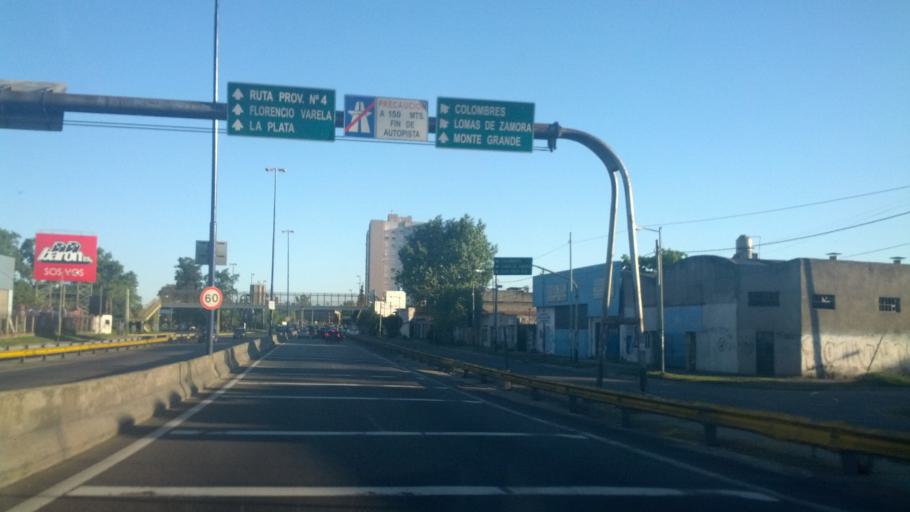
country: AR
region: Buenos Aires
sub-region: Partido de Lomas de Zamora
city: Lomas de Zamora
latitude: -34.7577
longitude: -58.4322
